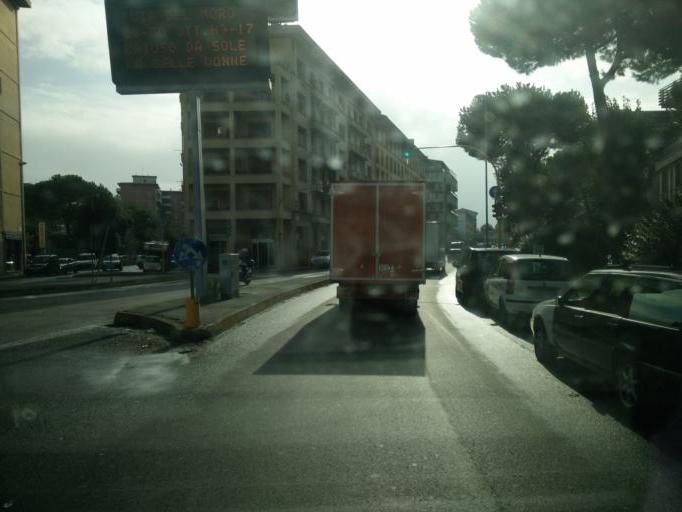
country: IT
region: Tuscany
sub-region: Province of Florence
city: Florence
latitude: 43.7901
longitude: 11.2230
